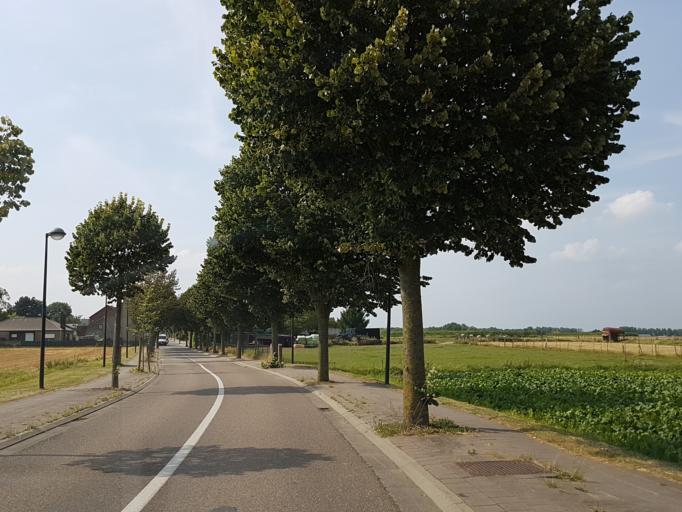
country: BE
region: Flanders
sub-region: Provincie Vlaams-Brabant
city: Kortenberg
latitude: 50.8979
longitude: 4.5822
